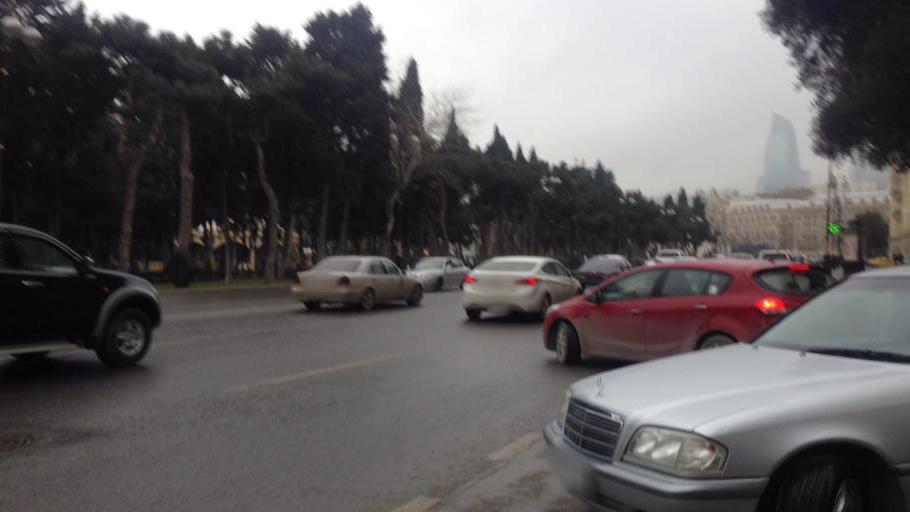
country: AZ
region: Baki
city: Badamdar
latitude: 40.3689
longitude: 49.8412
